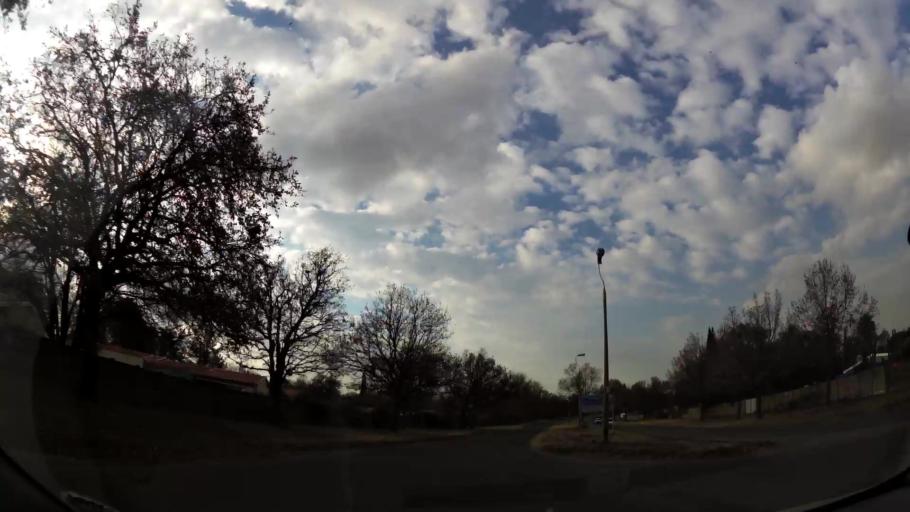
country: ZA
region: Orange Free State
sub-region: Fezile Dabi District Municipality
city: Sasolburg
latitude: -26.8138
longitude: 27.8194
